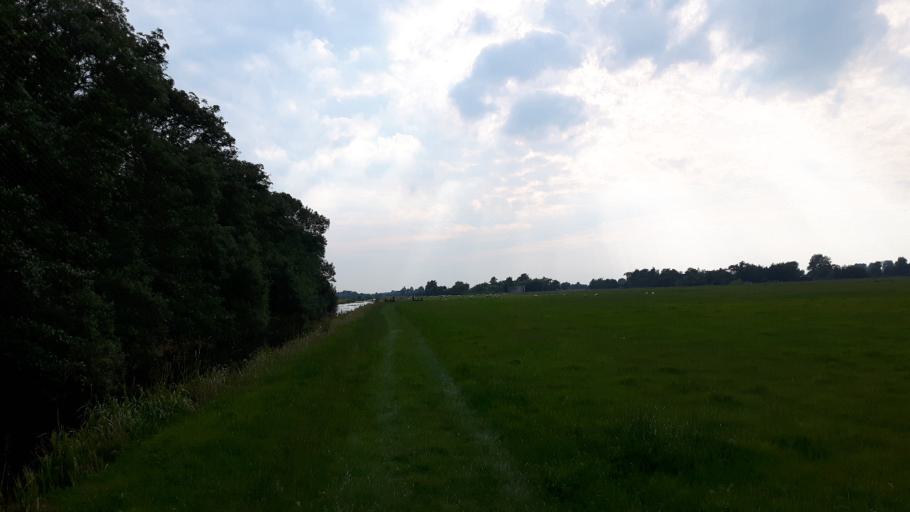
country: NL
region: Utrecht
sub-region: Gemeente Woerden
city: Woerden
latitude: 52.1334
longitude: 4.9104
